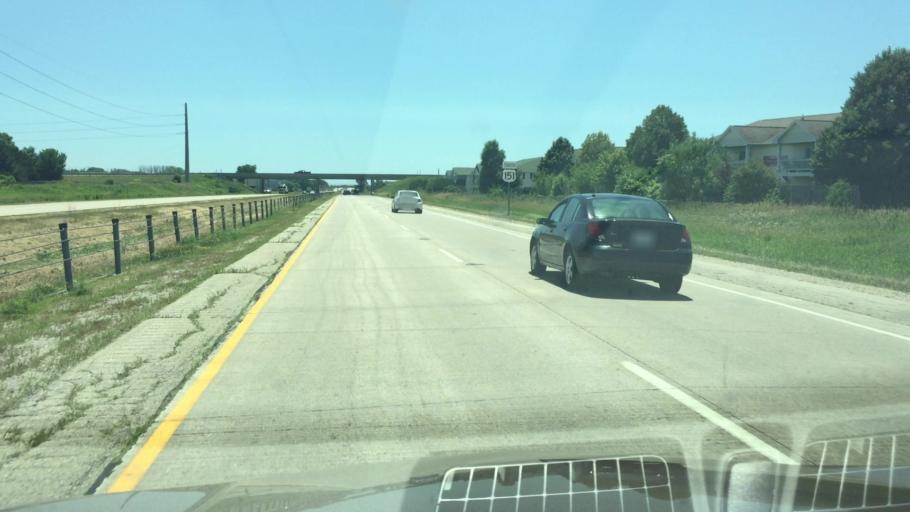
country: US
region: Wisconsin
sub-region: Dodge County
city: Beaver Dam
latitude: 43.4799
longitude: -88.8155
